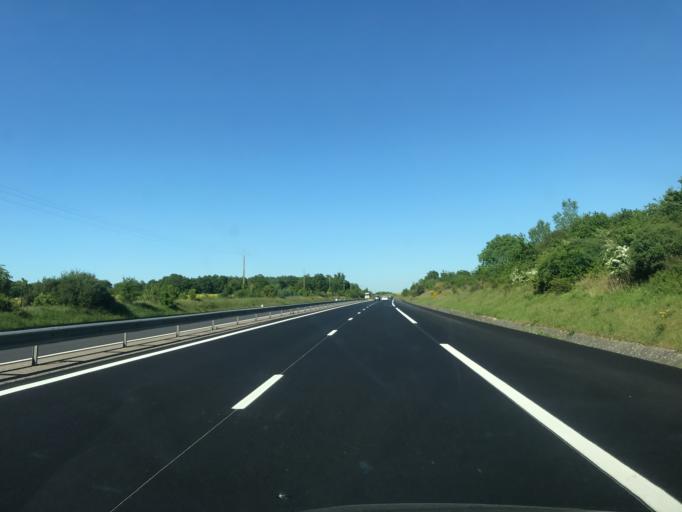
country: FR
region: Haute-Normandie
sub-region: Departement de l'Eure
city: Damville
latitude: 48.9096
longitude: 1.1809
